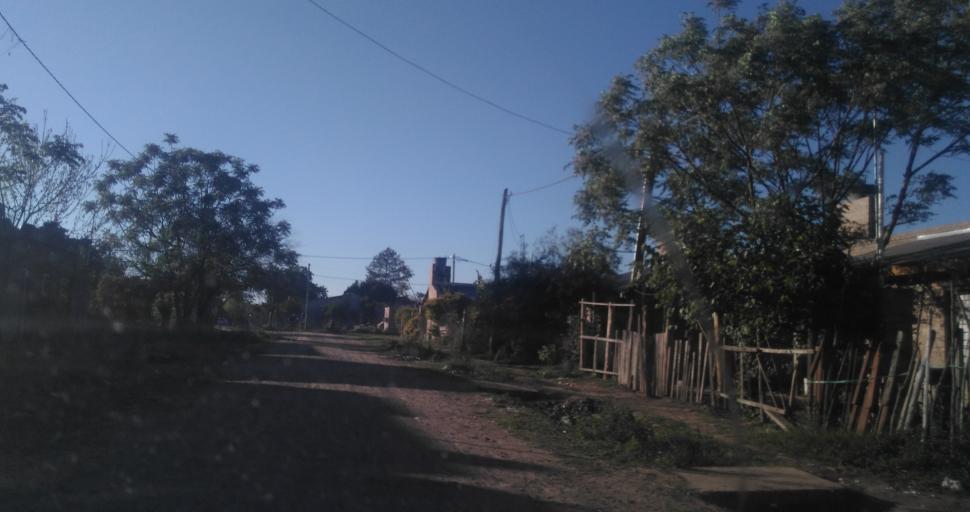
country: AR
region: Chaco
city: Fontana
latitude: -27.4238
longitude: -59.0237
